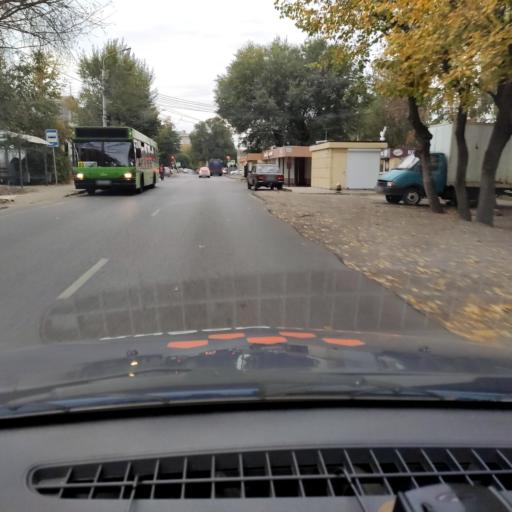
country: RU
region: Voronezj
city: Voronezh
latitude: 51.6352
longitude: 39.1888
